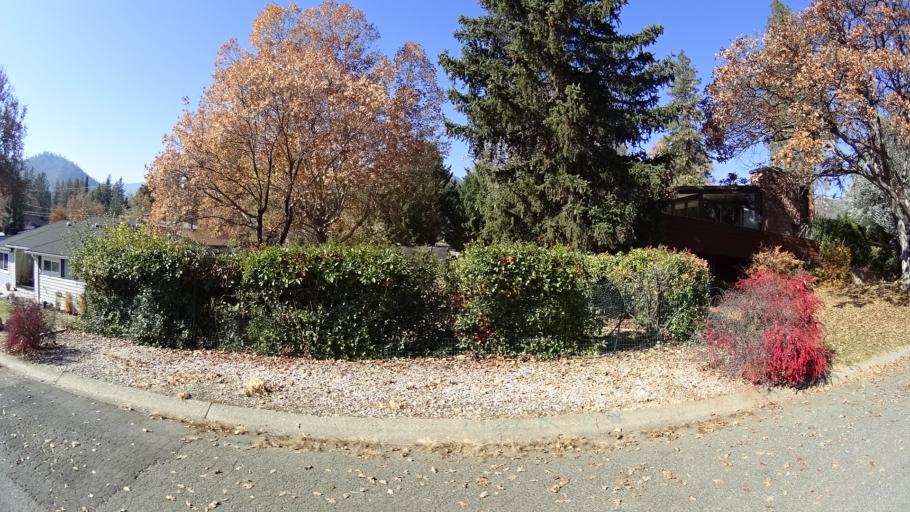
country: US
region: California
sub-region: Siskiyou County
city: Yreka
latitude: 41.7390
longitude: -122.6486
